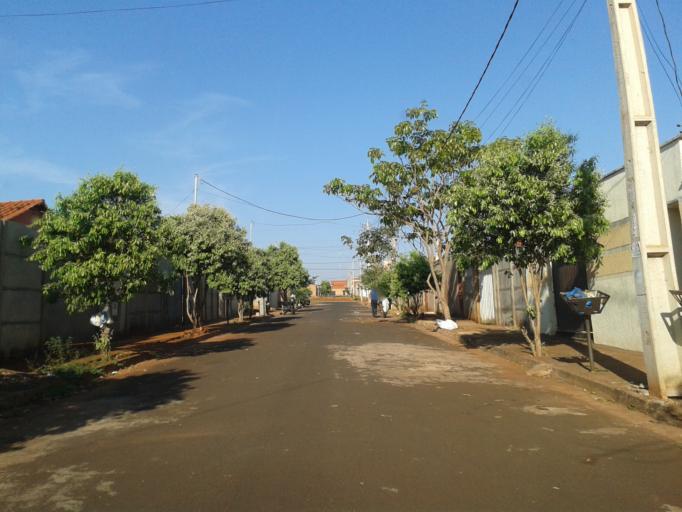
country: BR
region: Minas Gerais
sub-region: Ituiutaba
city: Ituiutaba
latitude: -18.9847
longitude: -49.4254
